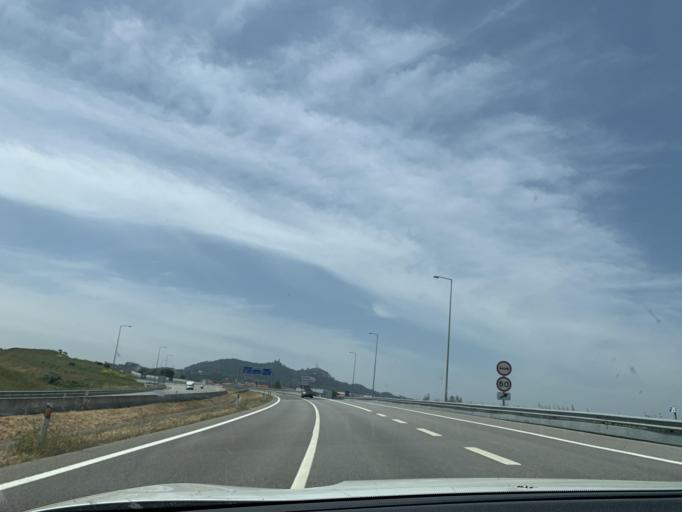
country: PT
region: Lisbon
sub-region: Sintra
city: Sintra
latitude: 38.8139
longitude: -9.3539
